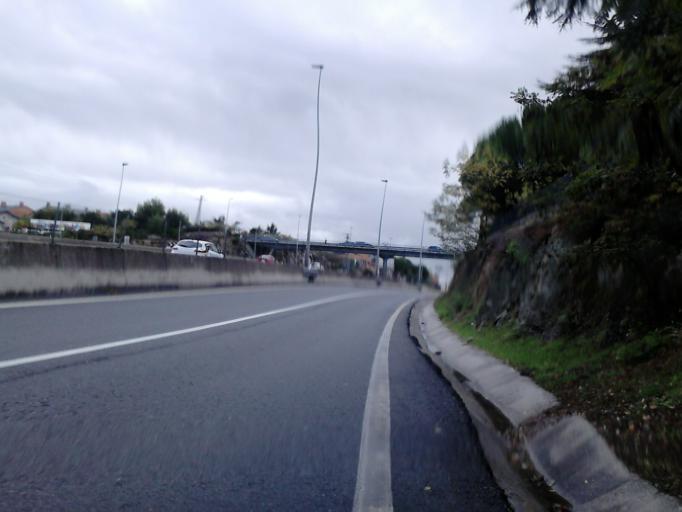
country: ES
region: Madrid
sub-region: Provincia de Madrid
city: Torrelodones
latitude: 40.5737
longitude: -3.9274
